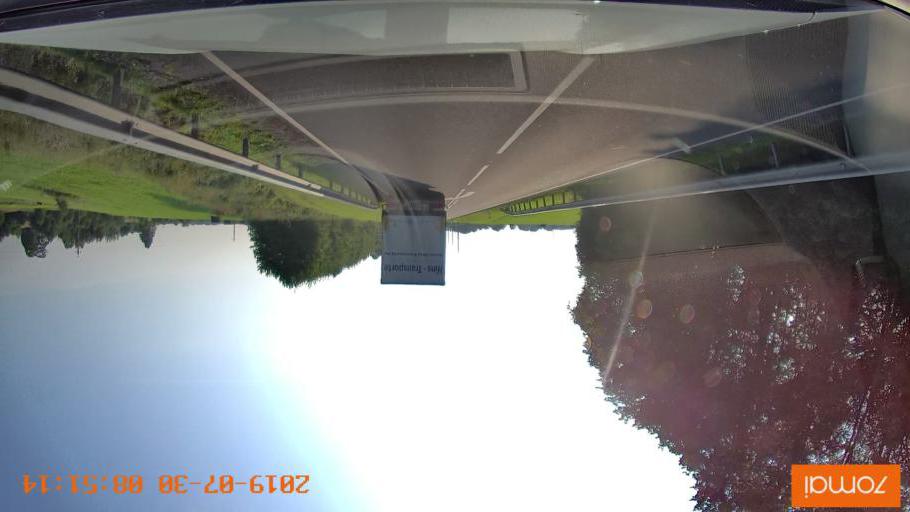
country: RU
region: Kaliningrad
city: Chernyakhovsk
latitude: 54.6035
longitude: 21.9540
